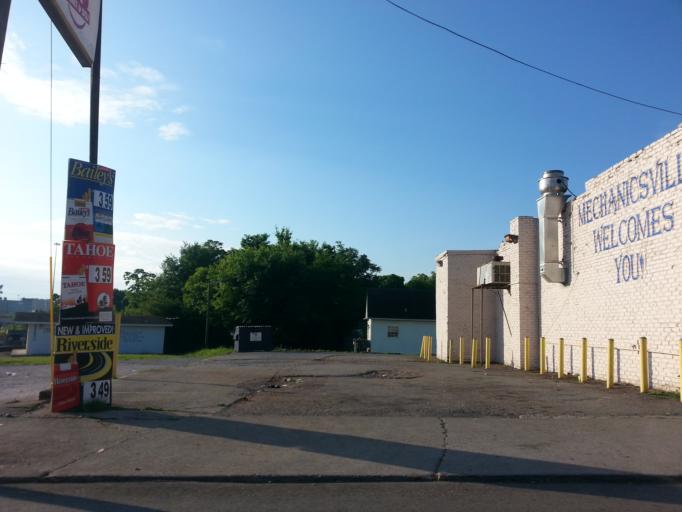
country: US
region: Tennessee
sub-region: Knox County
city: Knoxville
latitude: 35.9718
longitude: -83.9337
